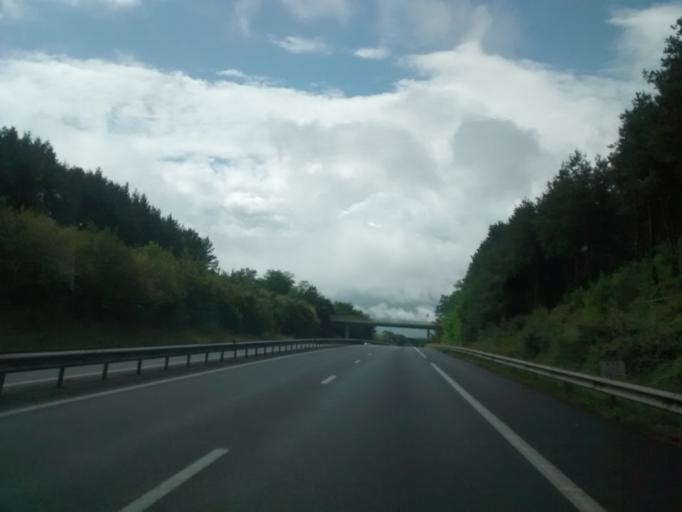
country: FR
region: Aquitaine
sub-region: Departement des Pyrenees-Atlantiques
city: Bardos
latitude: 43.4945
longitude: -1.2458
